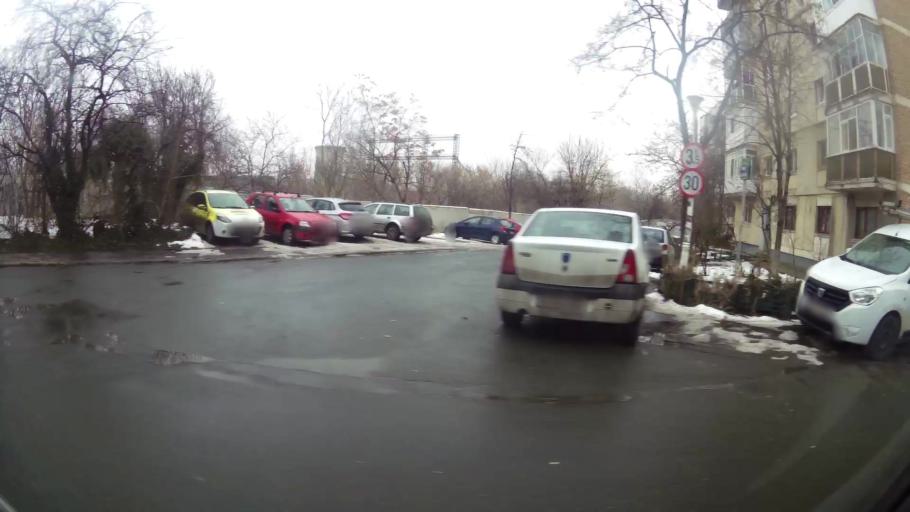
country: RO
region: Ilfov
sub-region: Comuna Chiajna
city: Rosu
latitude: 44.4374
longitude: 26.0422
